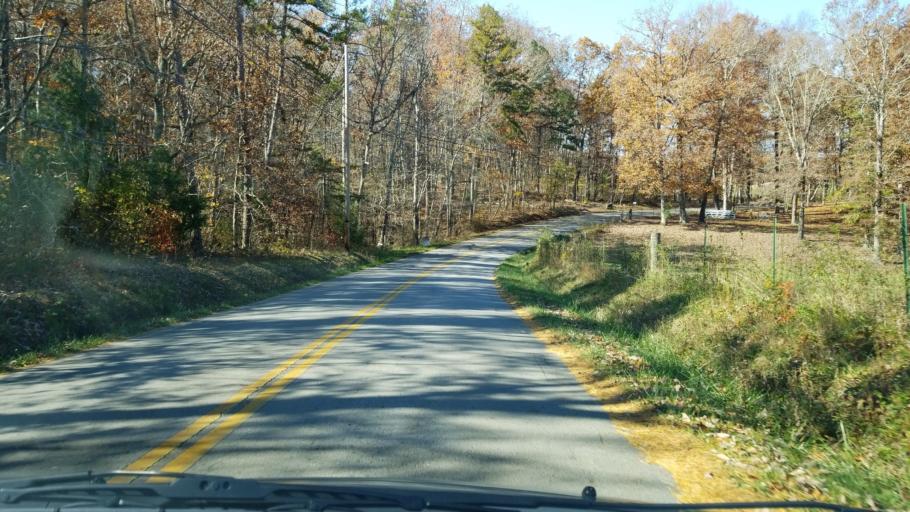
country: US
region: Tennessee
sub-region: Hamilton County
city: Falling Water
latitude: 35.2185
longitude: -85.2747
